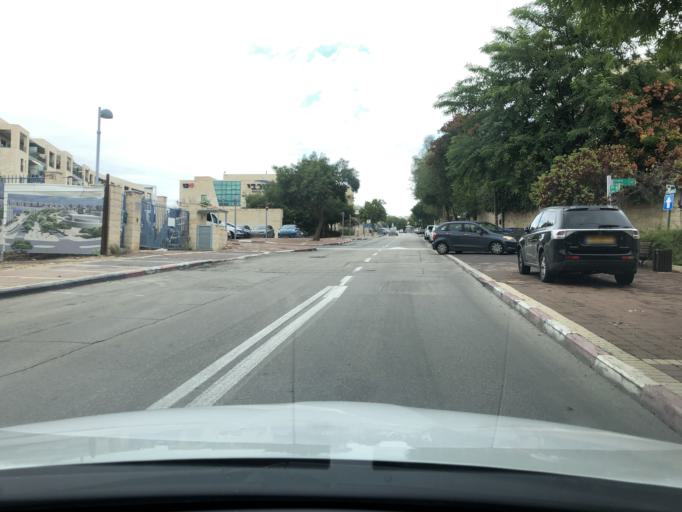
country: IL
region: Central District
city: Modiin
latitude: 31.9042
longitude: 35.0080
